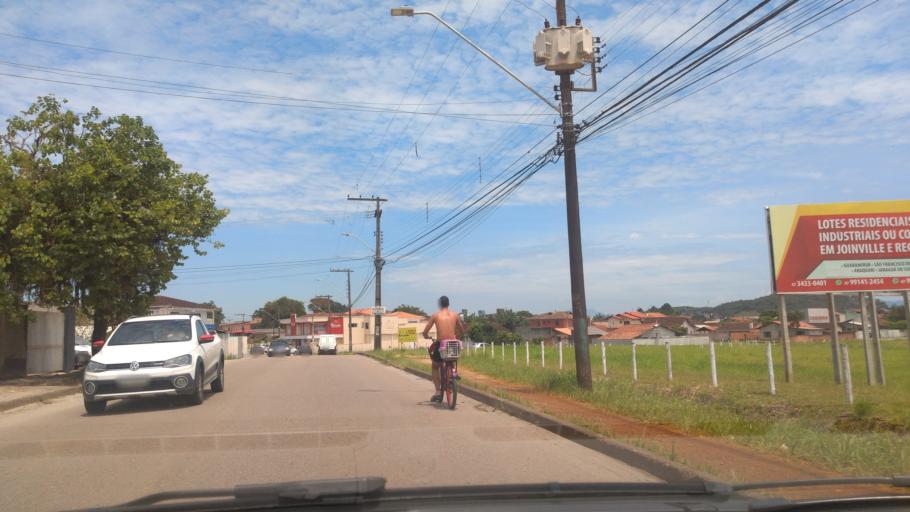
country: BR
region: Santa Catarina
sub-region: Joinville
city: Joinville
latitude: -26.3268
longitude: -48.8094
